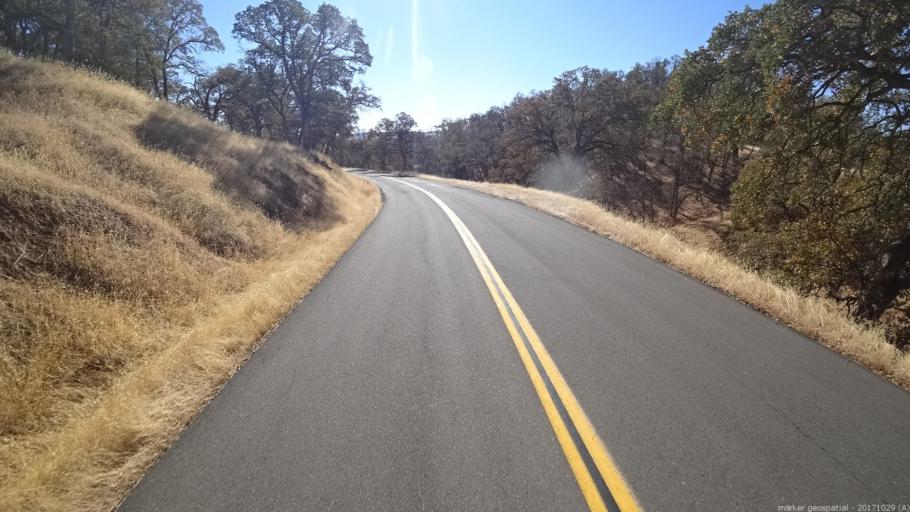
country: US
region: California
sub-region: Shasta County
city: Shasta
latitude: 40.4409
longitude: -122.6683
